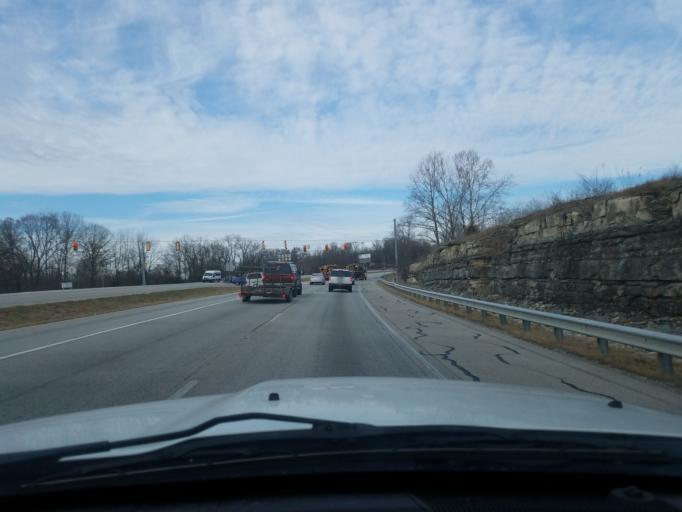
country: US
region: Indiana
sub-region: Lawrence County
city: Oolitic
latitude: 38.9092
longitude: -86.5444
